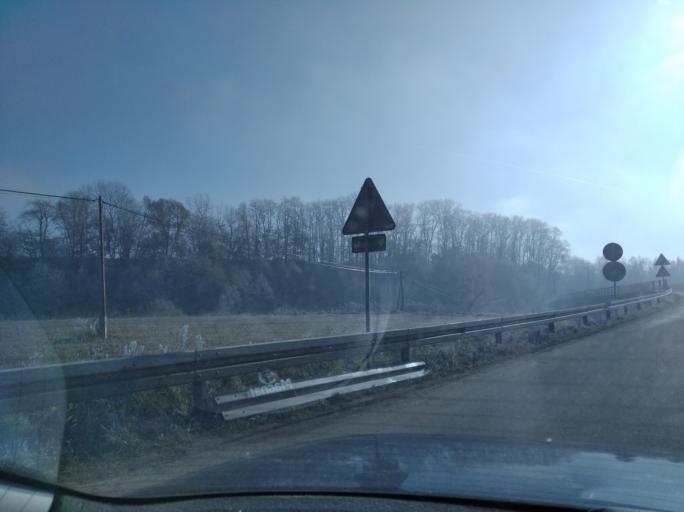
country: PL
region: Subcarpathian Voivodeship
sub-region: Powiat strzyzowski
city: Wysoka Strzyzowska
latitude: 49.8656
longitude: 21.7070
